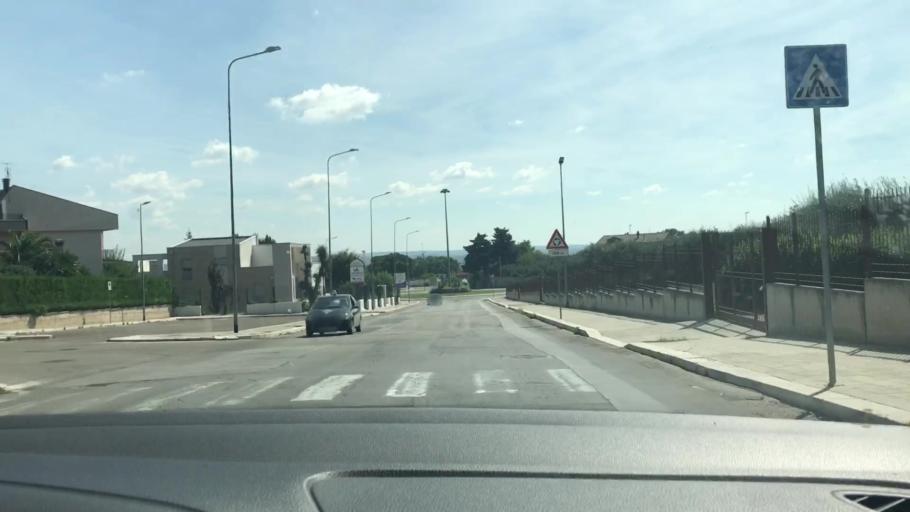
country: IT
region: Apulia
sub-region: Provincia di Bari
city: Altamura
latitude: 40.8259
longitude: 16.5648
